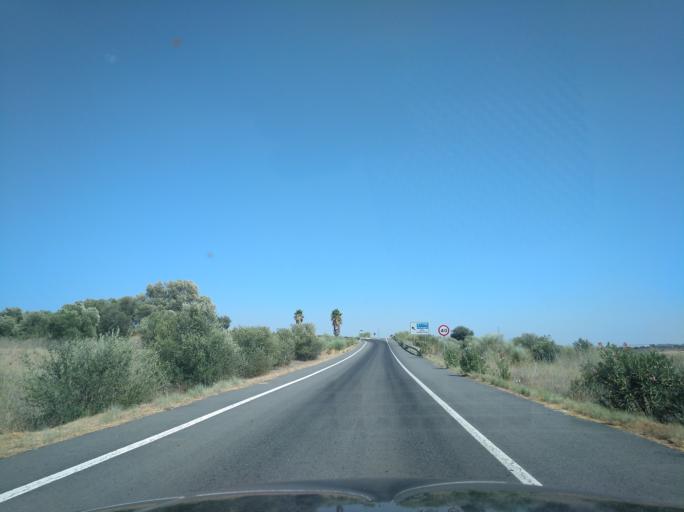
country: ES
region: Andalusia
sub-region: Provincia de Huelva
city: Aljaraque
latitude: 37.3345
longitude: -7.0246
